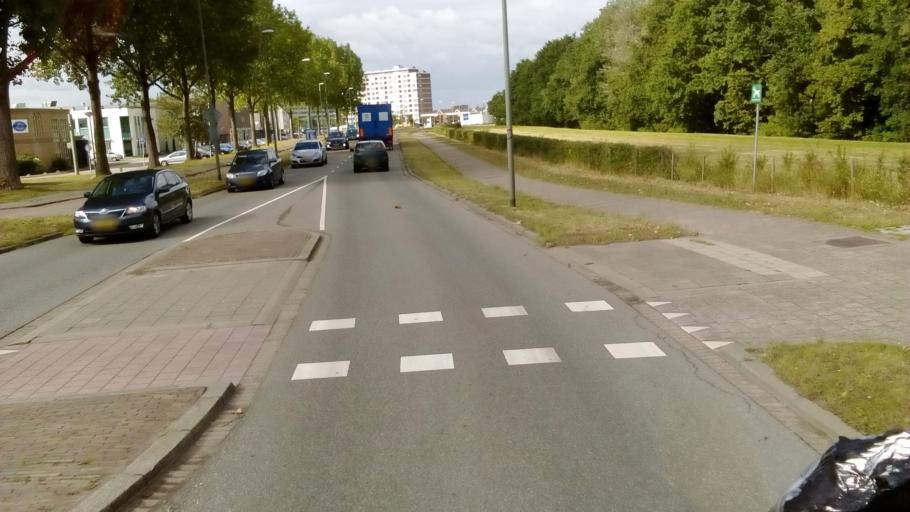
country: NL
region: South Holland
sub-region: Gemeente Schiedam
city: Schiedam
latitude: 51.9091
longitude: 4.3833
